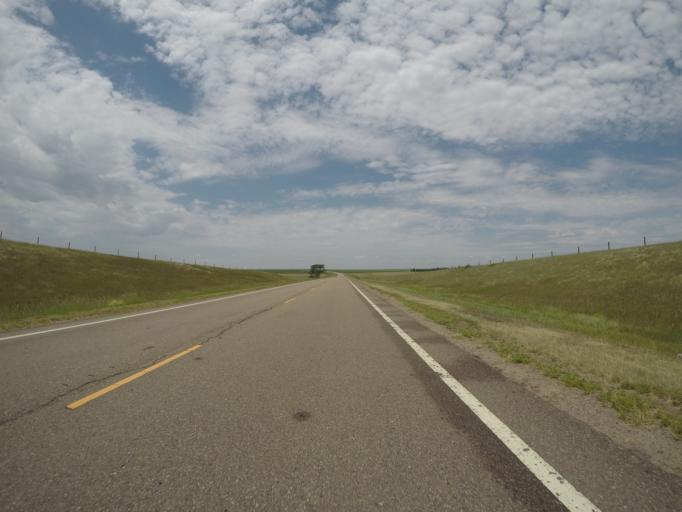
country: US
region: Kansas
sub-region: Thomas County
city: Colby
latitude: 39.3884
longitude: -100.8272
